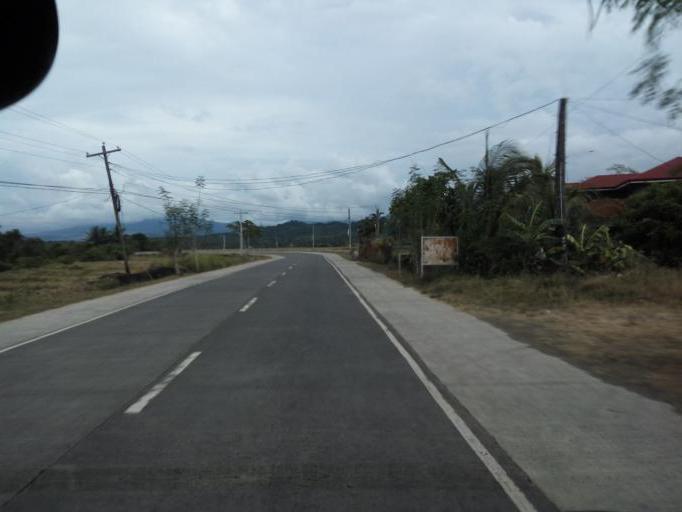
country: PH
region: Cagayan Valley
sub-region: Province of Cagayan
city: Gonzaga
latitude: 18.2430
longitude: 121.9616
